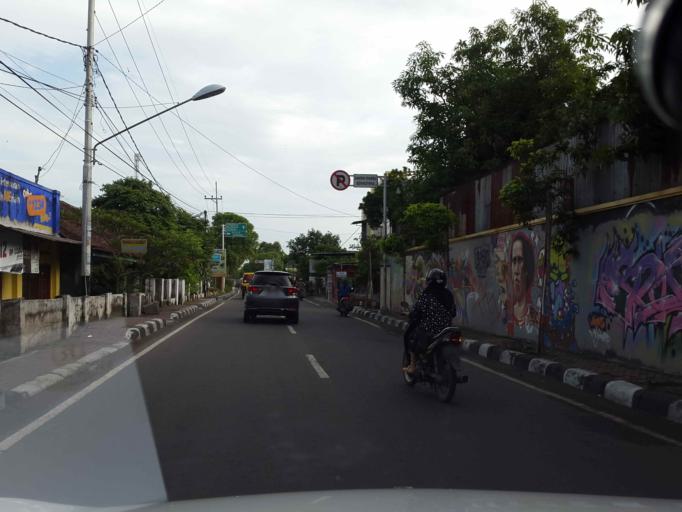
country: ID
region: East Java
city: Soko
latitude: -7.4813
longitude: 112.4285
